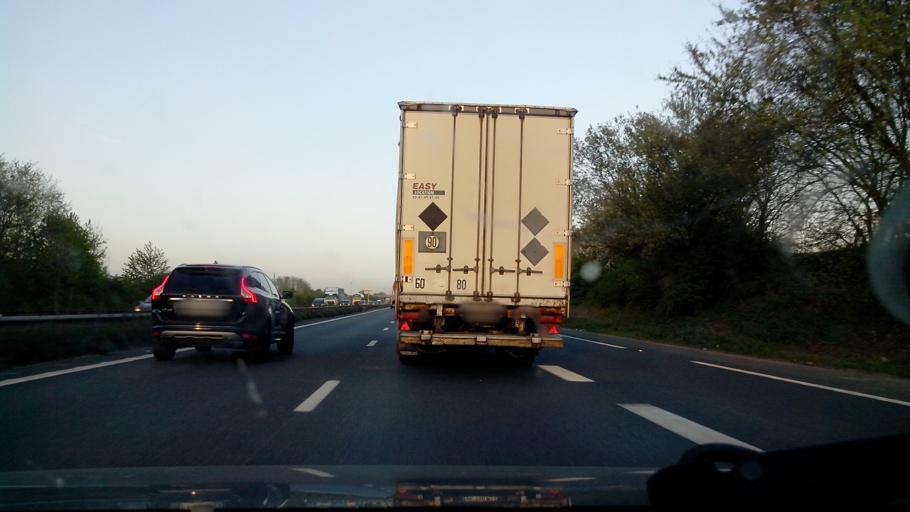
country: FR
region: Ile-de-France
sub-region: Departement de Seine-et-Marne
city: Lieusaint
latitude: 48.6445
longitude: 2.5417
